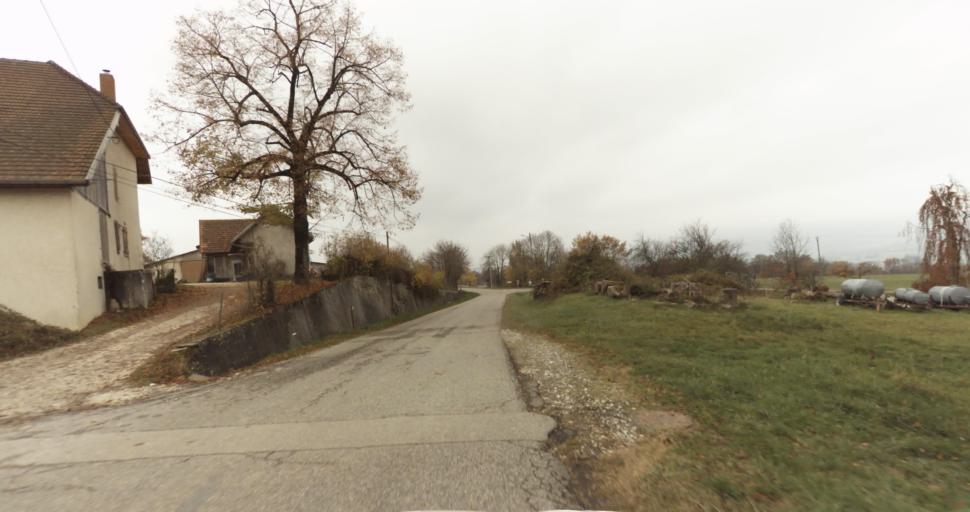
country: FR
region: Rhone-Alpes
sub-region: Departement de la Haute-Savoie
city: Saint-Felix
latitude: 45.7731
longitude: 5.9868
